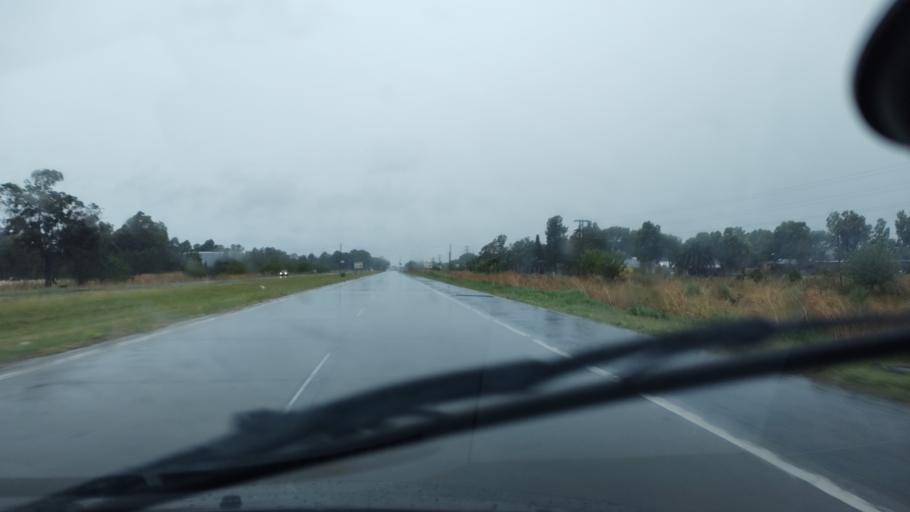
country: AR
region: Buenos Aires
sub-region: Partido de San Vicente
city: San Vicente
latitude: -35.0579
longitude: -58.4494
